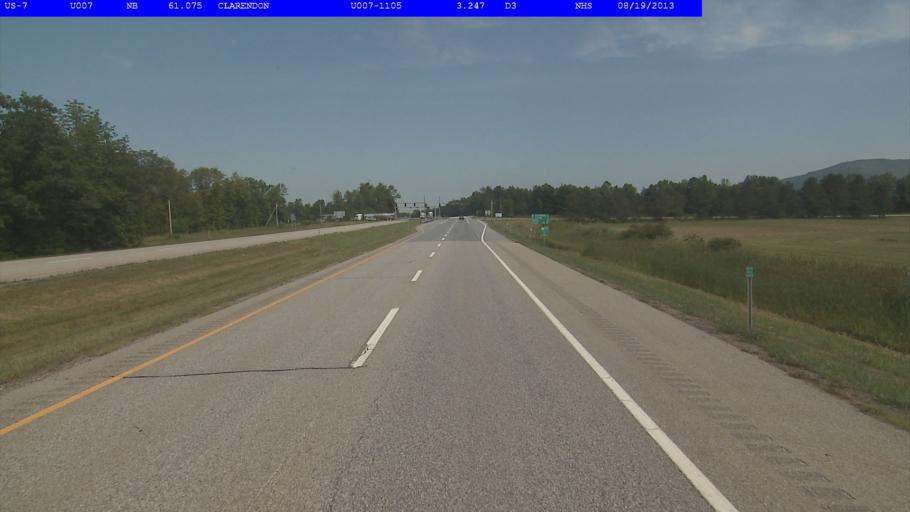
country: US
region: Vermont
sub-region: Rutland County
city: Rutland
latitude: 43.5388
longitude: -72.9577
